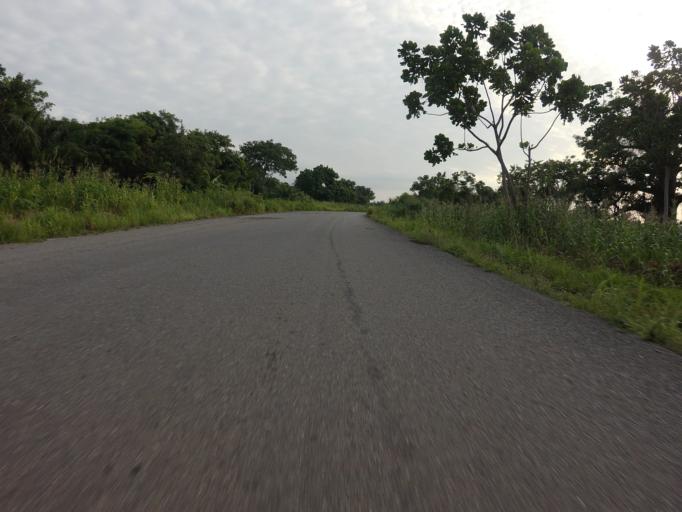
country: GH
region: Volta
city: Kpandu
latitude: 6.8679
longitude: 0.4113
